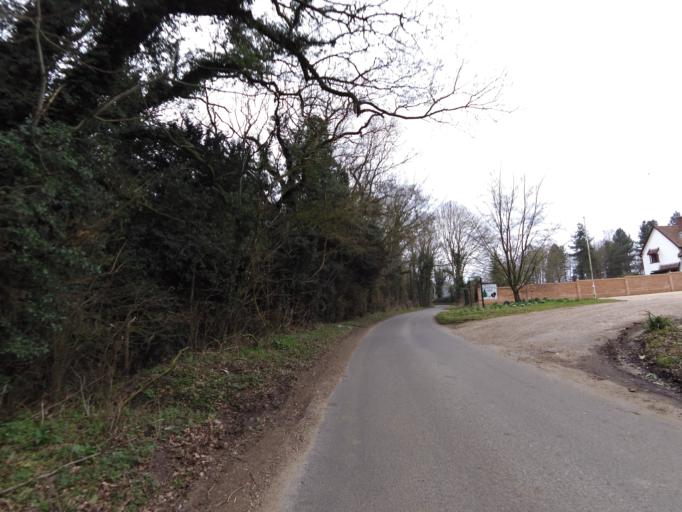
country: GB
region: England
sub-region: Suffolk
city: Halesworth
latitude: 52.3510
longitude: 1.5269
